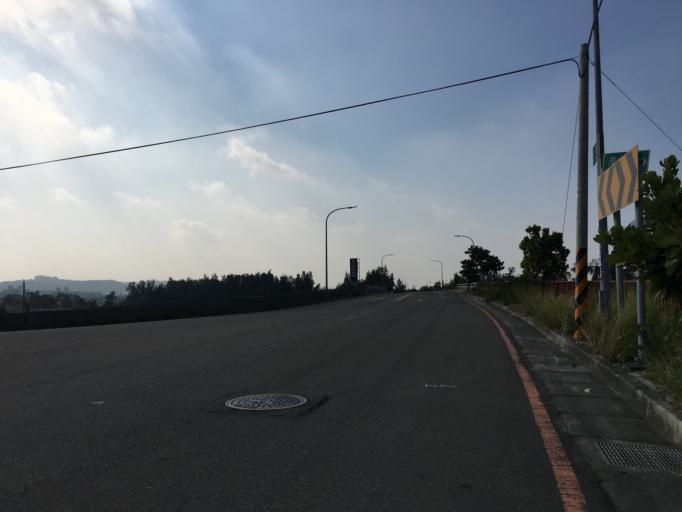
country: TW
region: Taiwan
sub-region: Hsinchu
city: Hsinchu
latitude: 24.8022
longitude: 120.9172
